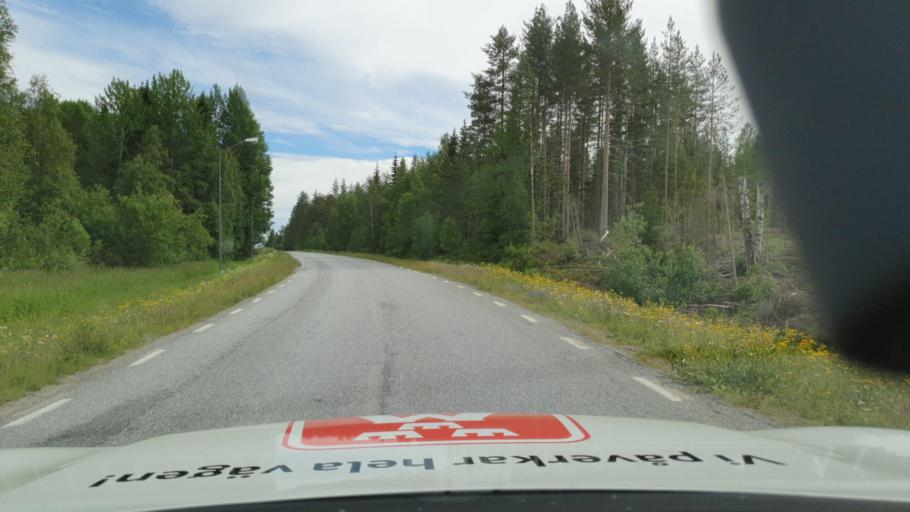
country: SE
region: Vaesterbotten
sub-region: Skelleftea Kommun
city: Burea
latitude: 64.4865
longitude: 21.0354
